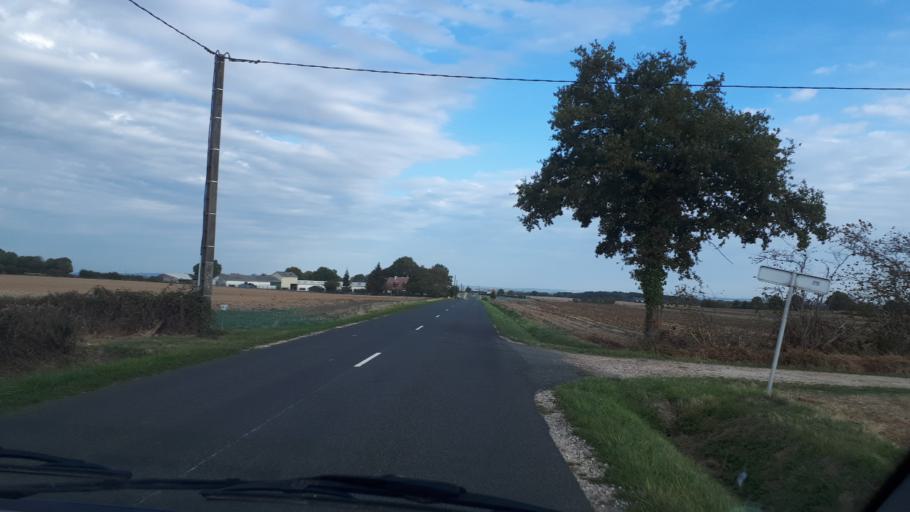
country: FR
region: Centre
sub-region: Departement du Loir-et-Cher
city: Mondoubleau
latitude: 47.9494
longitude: 0.9321
